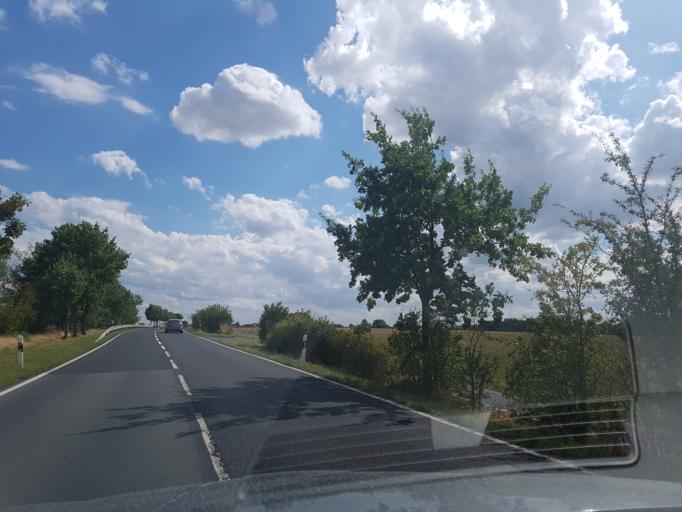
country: DE
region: Saxony
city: Grossenhain
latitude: 51.2734
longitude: 13.5330
